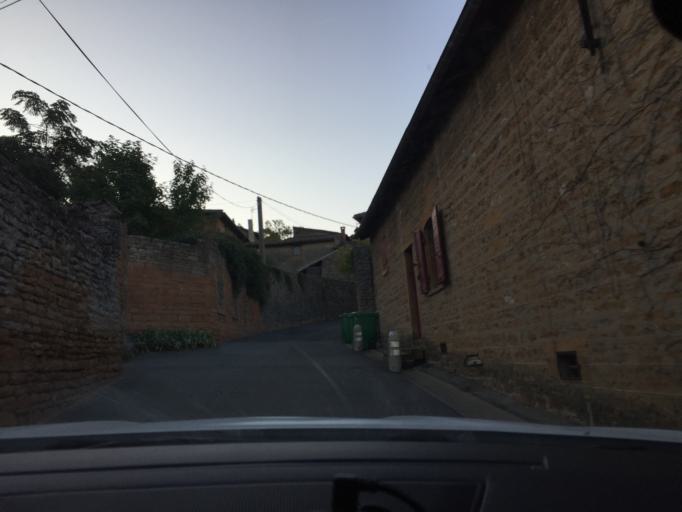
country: FR
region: Rhone-Alpes
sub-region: Departement du Rhone
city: Charnay
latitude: 45.8922
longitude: 4.6675
